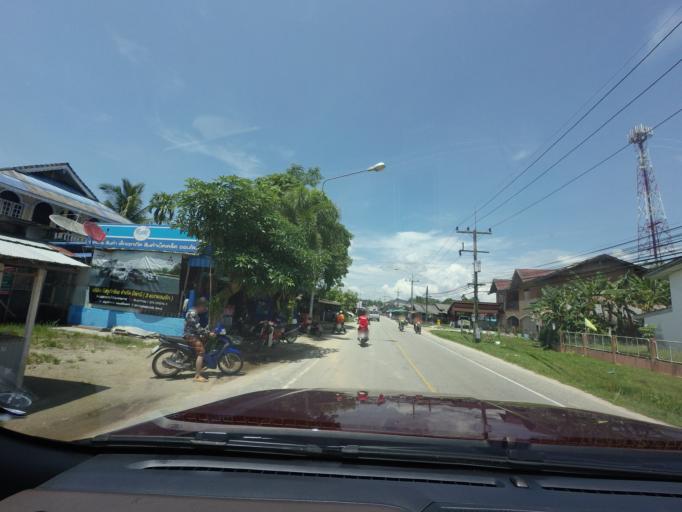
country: TH
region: Narathiwat
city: Chanae
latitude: 6.1304
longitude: 101.6976
